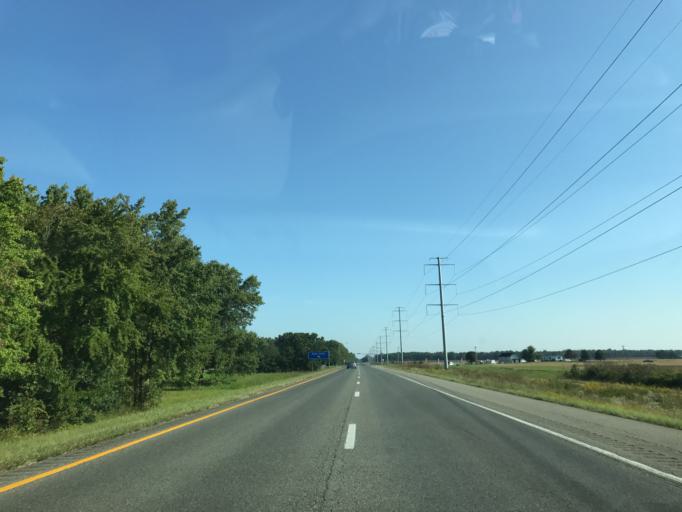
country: US
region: Maryland
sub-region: Queen Anne's County
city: Centreville
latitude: 39.0762
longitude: -75.9801
